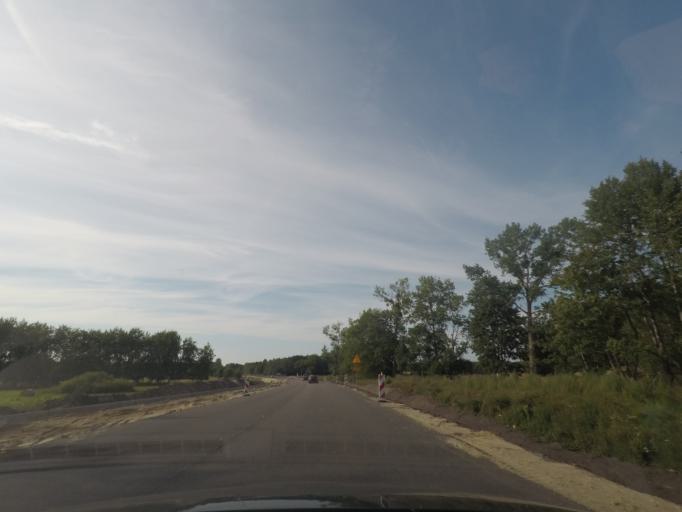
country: PL
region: Pomeranian Voivodeship
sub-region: Powiat leborski
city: Leba
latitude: 54.7271
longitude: 17.5688
